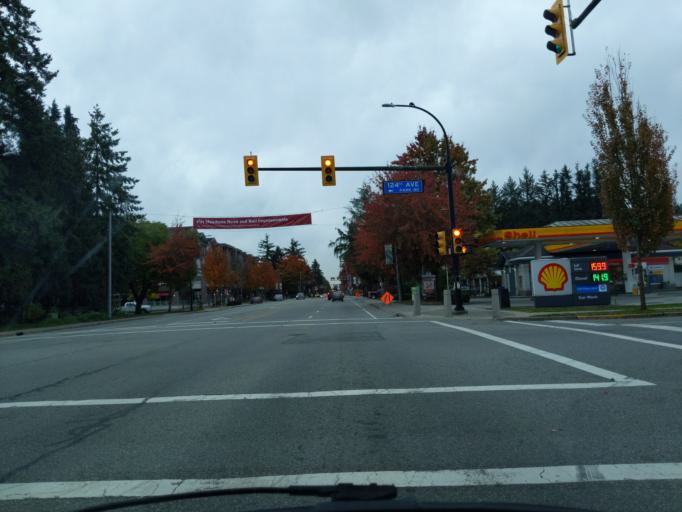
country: CA
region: British Columbia
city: Pitt Meadows
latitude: 49.2282
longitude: -122.6896
